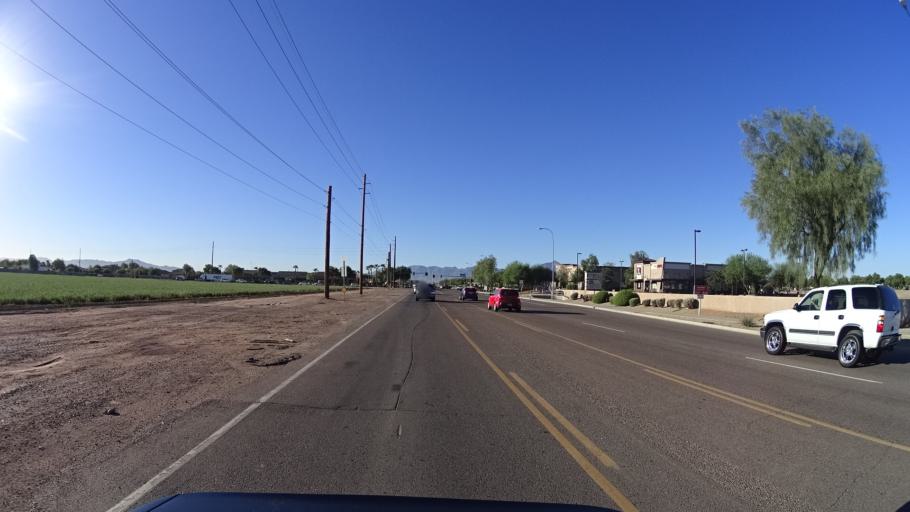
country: US
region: Arizona
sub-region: Maricopa County
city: Tolleson
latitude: 33.4245
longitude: -112.2212
